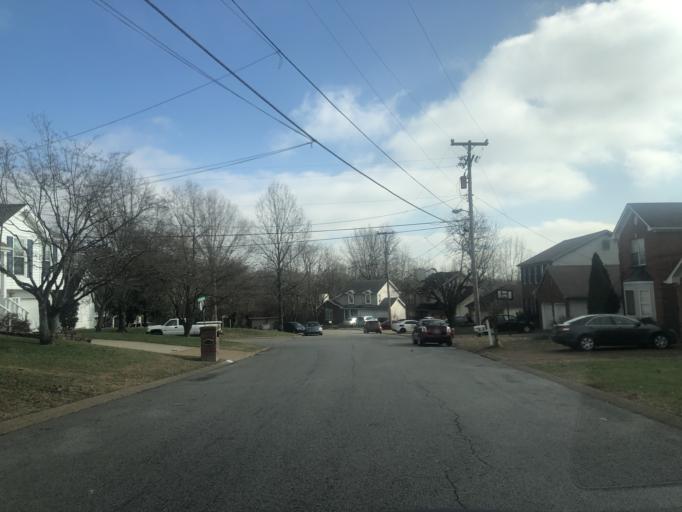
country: US
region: Tennessee
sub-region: Rutherford County
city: La Vergne
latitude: 36.0843
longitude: -86.6548
